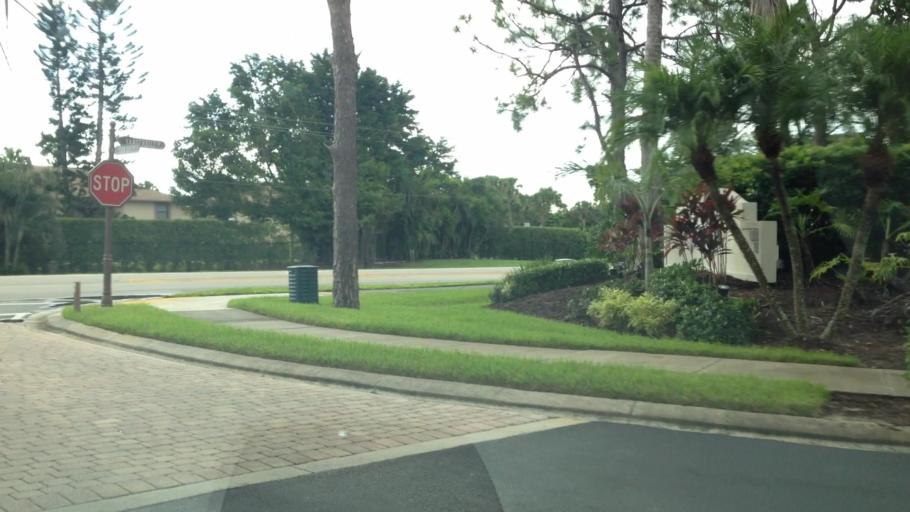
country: US
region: Florida
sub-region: Collier County
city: Naples Park
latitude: 26.3047
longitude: -81.8191
